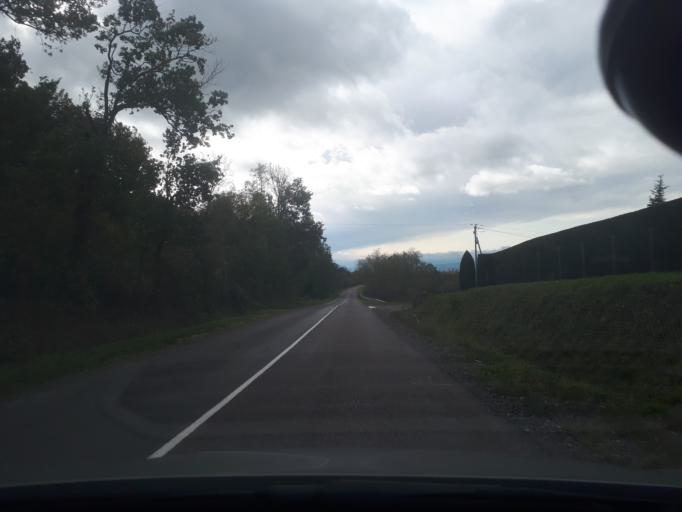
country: FR
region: Rhone-Alpes
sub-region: Departement de la Loire
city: Bellegarde-en-Forez
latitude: 45.6854
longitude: 4.3004
